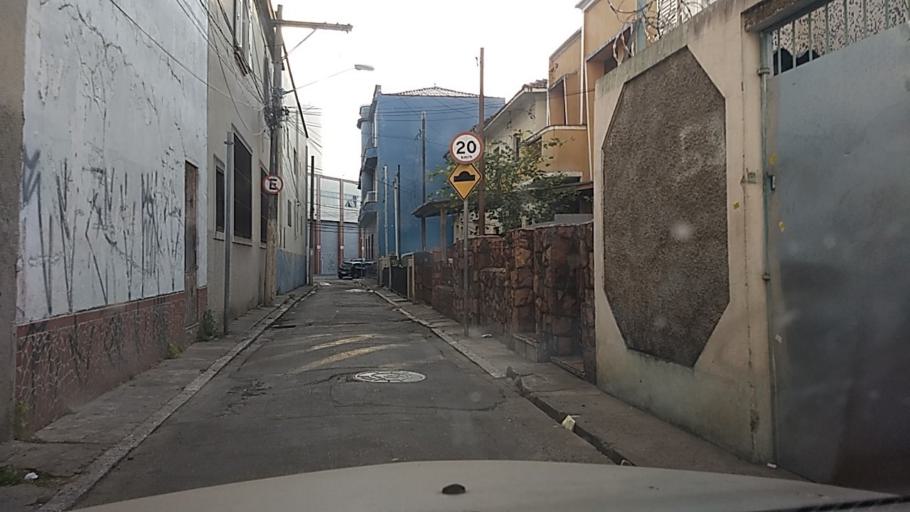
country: BR
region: Sao Paulo
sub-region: Sao Paulo
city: Sao Paulo
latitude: -23.5266
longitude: -46.6193
